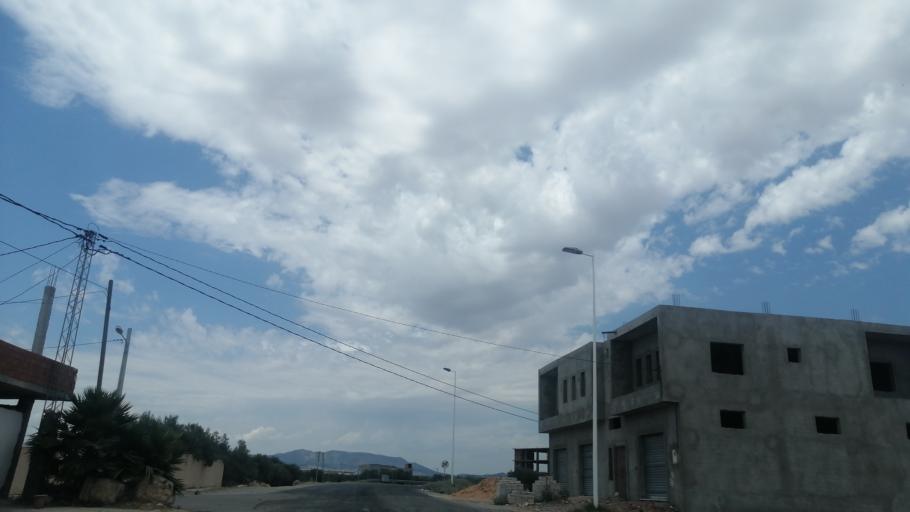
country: TN
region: Al Qayrawan
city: Sbikha
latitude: 36.1288
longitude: 10.0926
